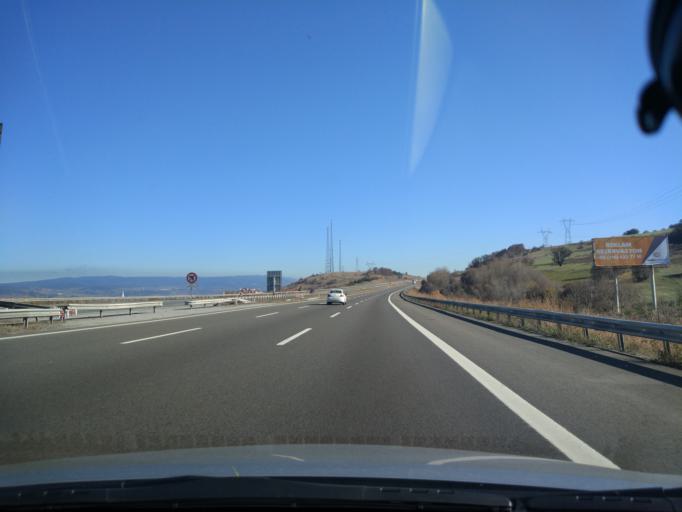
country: TR
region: Bolu
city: Yenicaga
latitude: 40.7650
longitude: 32.0198
